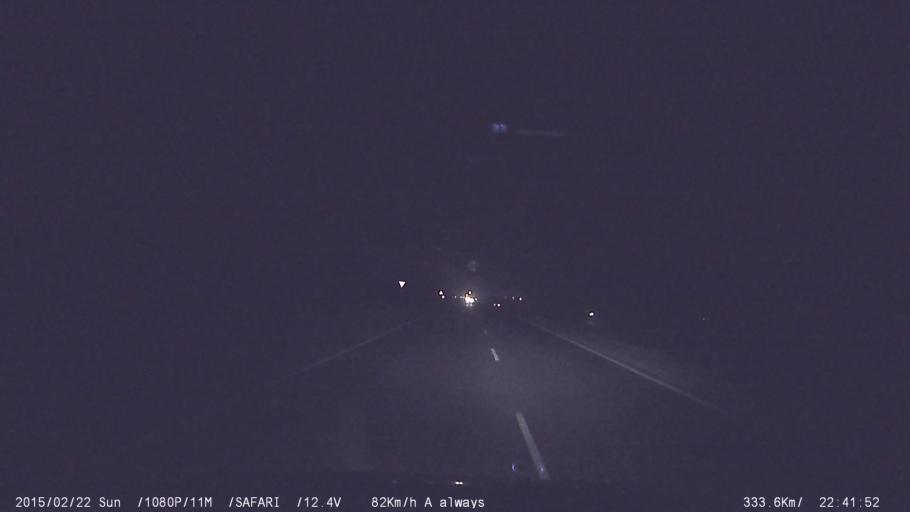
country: IN
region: Tamil Nadu
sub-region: Namakkal
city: Namakkal
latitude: 11.1858
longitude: 78.0756
